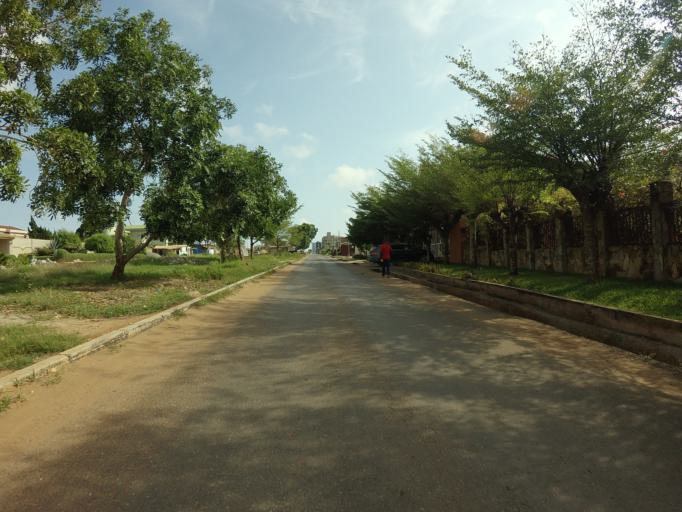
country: GH
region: Greater Accra
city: Nungua
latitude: 5.6395
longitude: -0.1007
